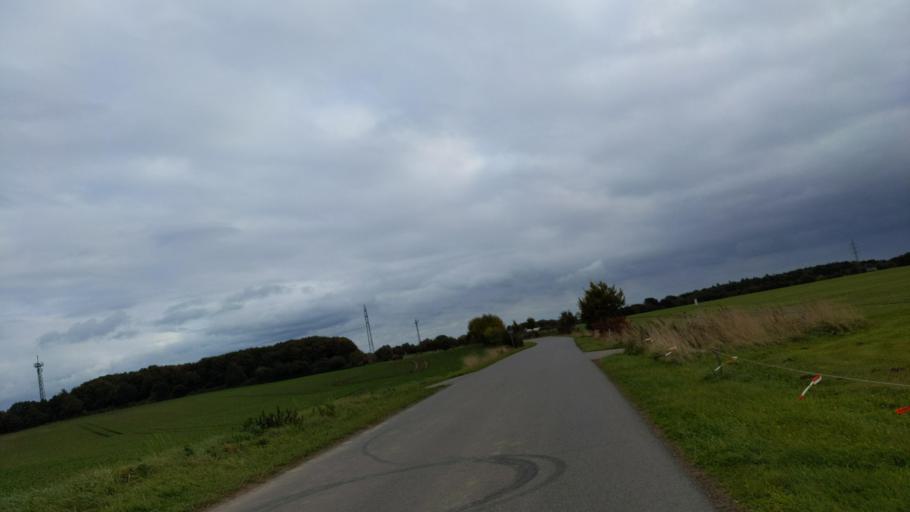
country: DE
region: Schleswig-Holstein
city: Sierksdorf
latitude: 54.0696
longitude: 10.7448
